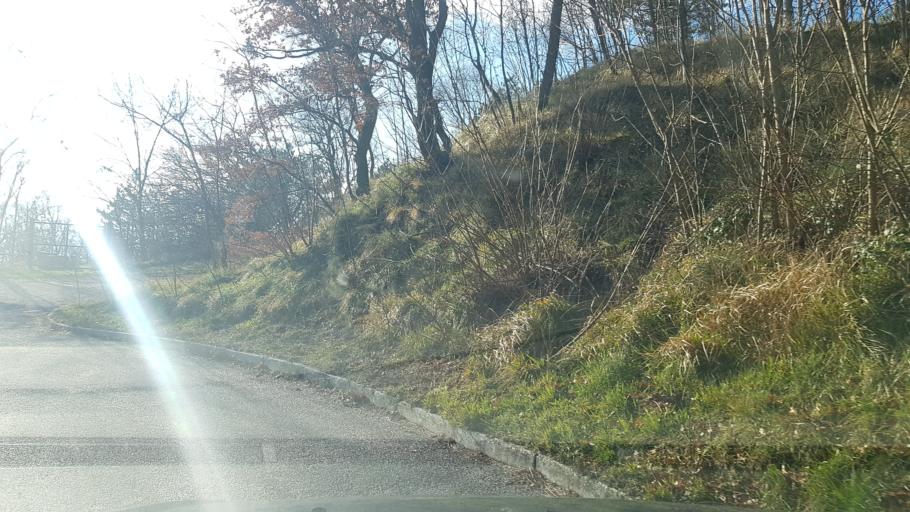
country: IT
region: Friuli Venezia Giulia
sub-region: Provincia di Trieste
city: Dolina
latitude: 45.6262
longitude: 13.8580
